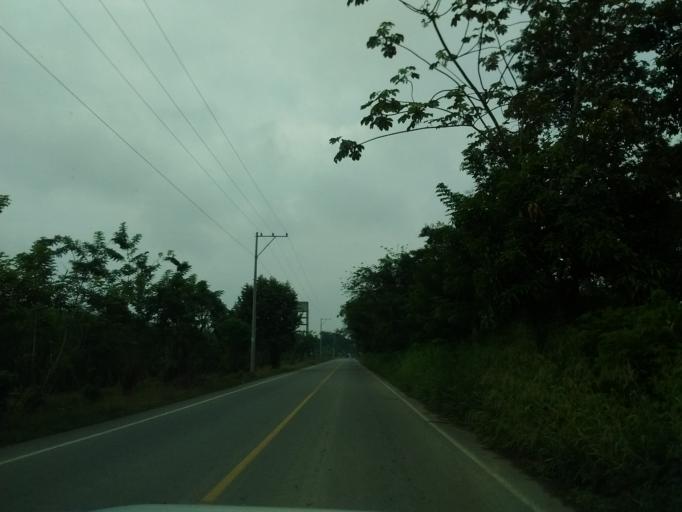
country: CO
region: Cauca
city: Padilla
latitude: 3.2256
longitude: -76.3550
